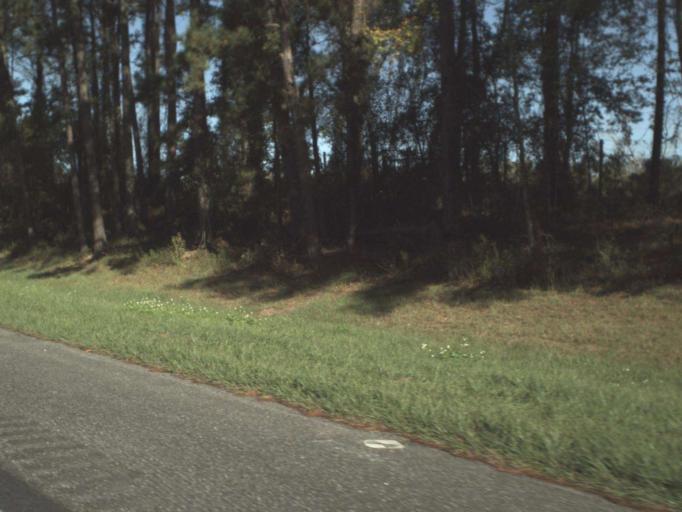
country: US
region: Florida
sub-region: Jefferson County
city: Monticello
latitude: 30.4488
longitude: -83.7478
